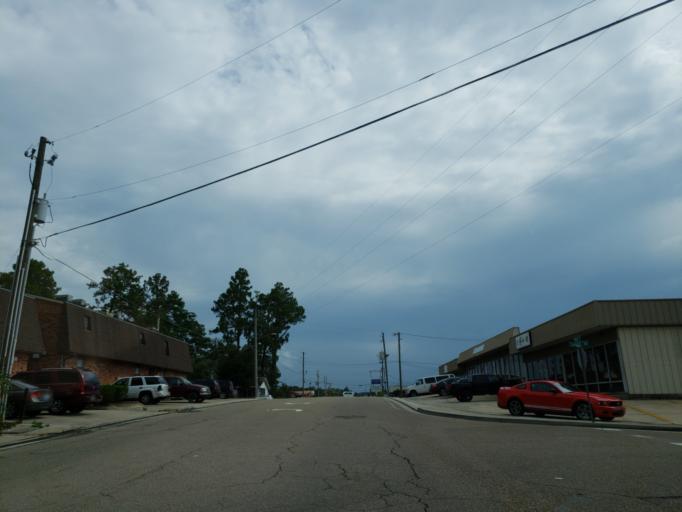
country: US
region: Mississippi
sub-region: Lamar County
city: Arnold Line
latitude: 31.3275
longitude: -89.3479
